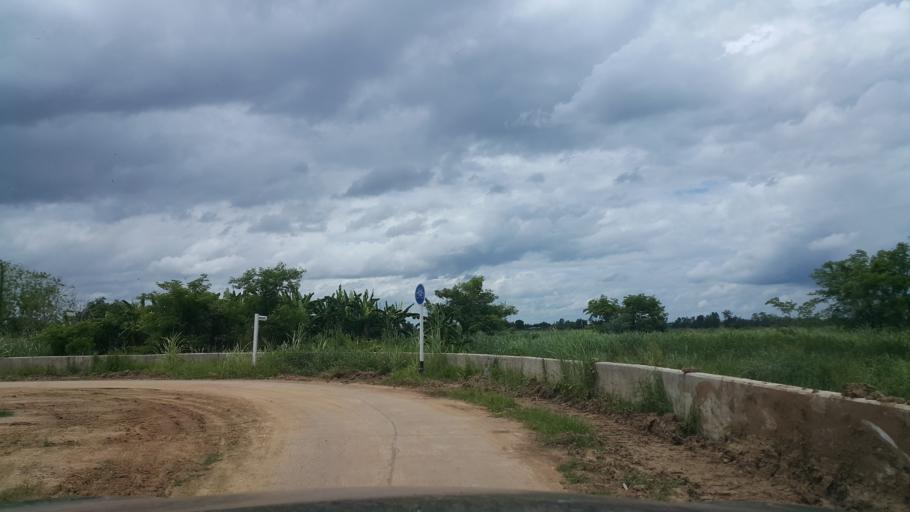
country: TH
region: Sukhothai
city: Sukhothai
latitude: 17.0205
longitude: 99.8020
